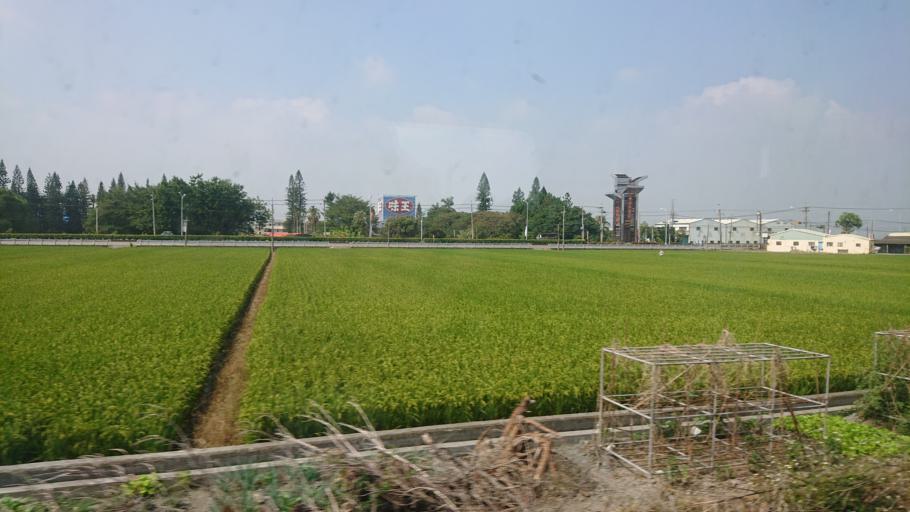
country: TW
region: Taiwan
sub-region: Yunlin
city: Douliu
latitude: 23.6418
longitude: 120.4713
